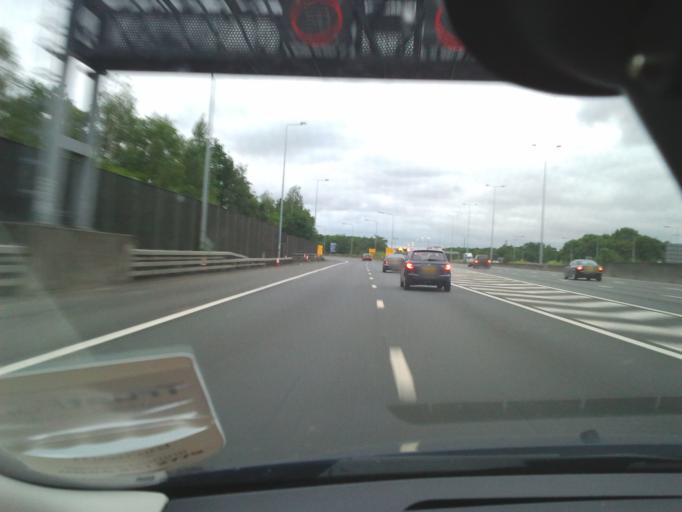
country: GB
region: England
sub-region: Surrey
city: Virginia Water
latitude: 51.4048
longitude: -0.5392
